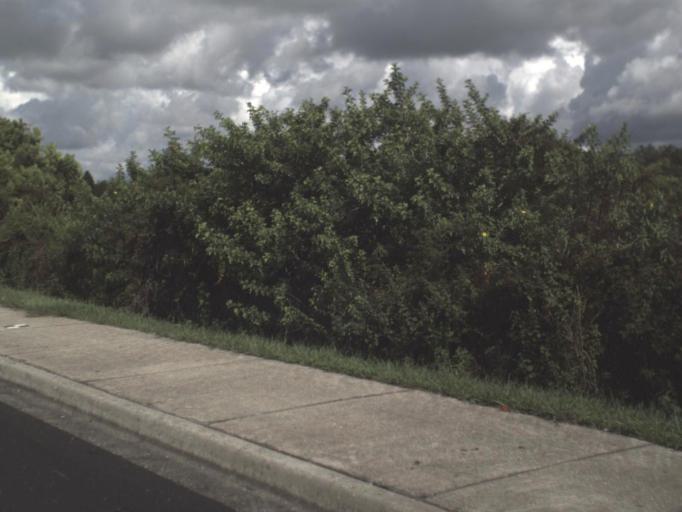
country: US
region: Florida
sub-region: Hillsborough County
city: Mango
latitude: 27.9816
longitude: -82.3154
